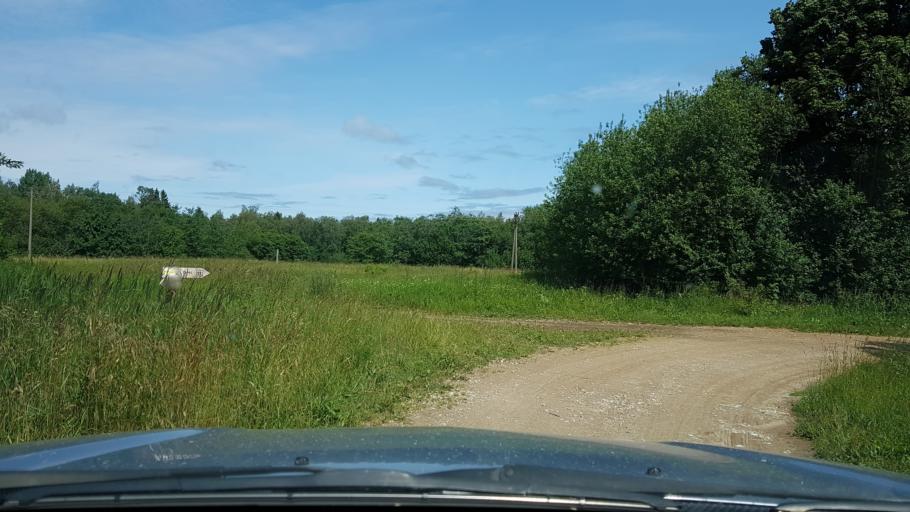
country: EE
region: Ida-Virumaa
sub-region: Sillamaee linn
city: Sillamae
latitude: 59.3665
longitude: 27.8144
